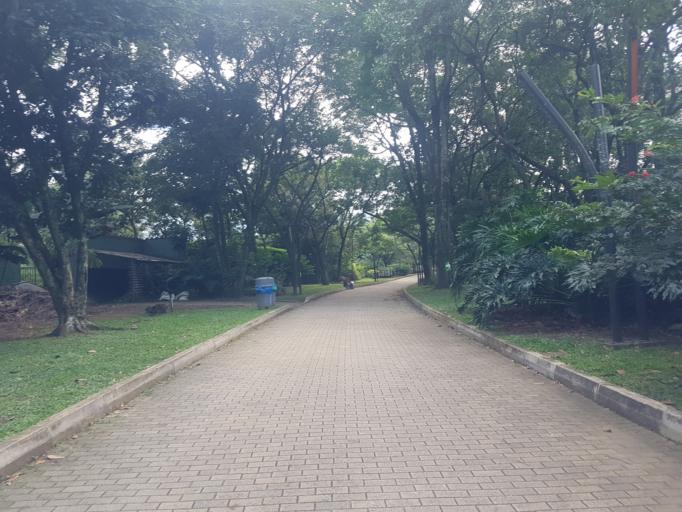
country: CO
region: Antioquia
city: Medellin
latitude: 6.2715
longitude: -75.5627
